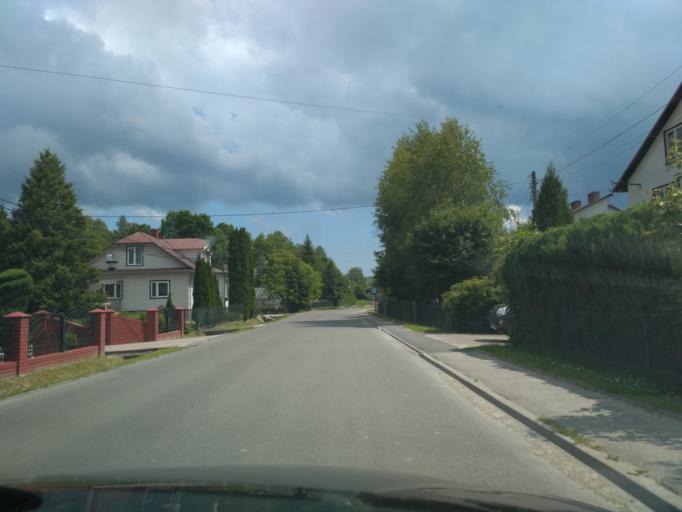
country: PL
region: Subcarpathian Voivodeship
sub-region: Powiat rzeszowski
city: Blazowa
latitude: 49.8796
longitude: 22.0873
